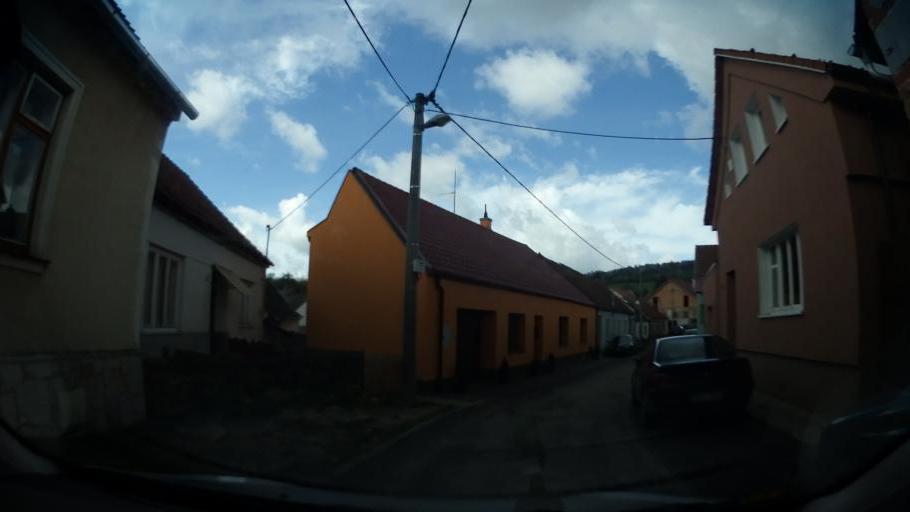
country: CZ
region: South Moravian
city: Ricany
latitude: 49.2373
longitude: 16.3986
